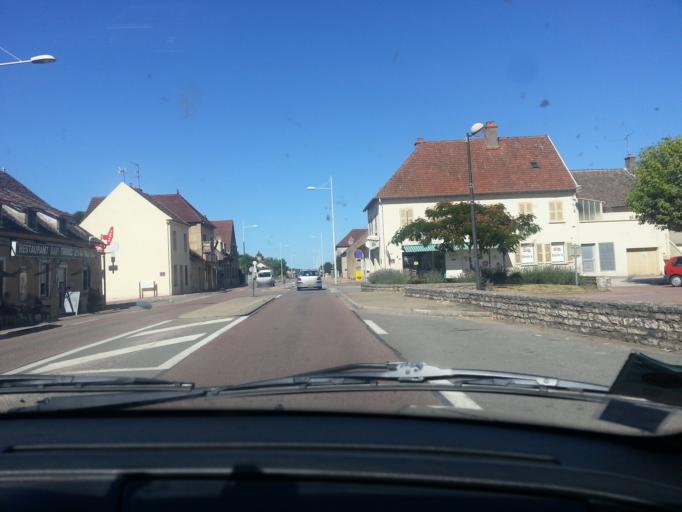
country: FR
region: Bourgogne
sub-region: Departement de Saone-et-Loire
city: Sassenay
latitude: 46.8196
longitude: 4.9673
